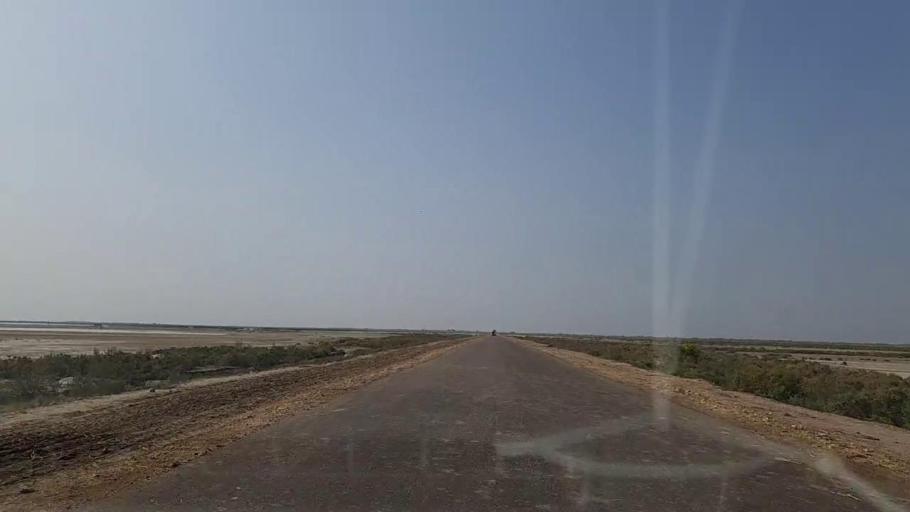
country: PK
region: Sindh
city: Chuhar Jamali
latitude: 24.2224
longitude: 67.8934
